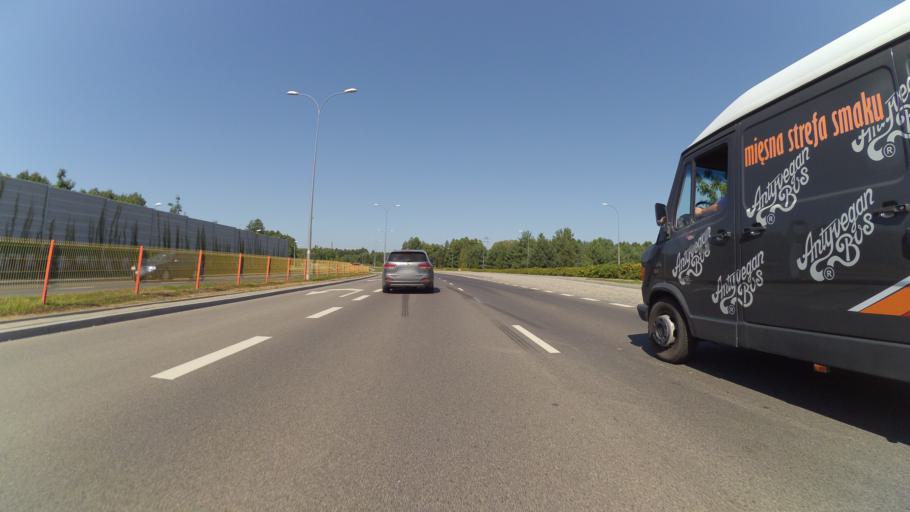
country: PL
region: Podlasie
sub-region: Bialystok
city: Bialystok
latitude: 53.1365
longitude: 23.2200
